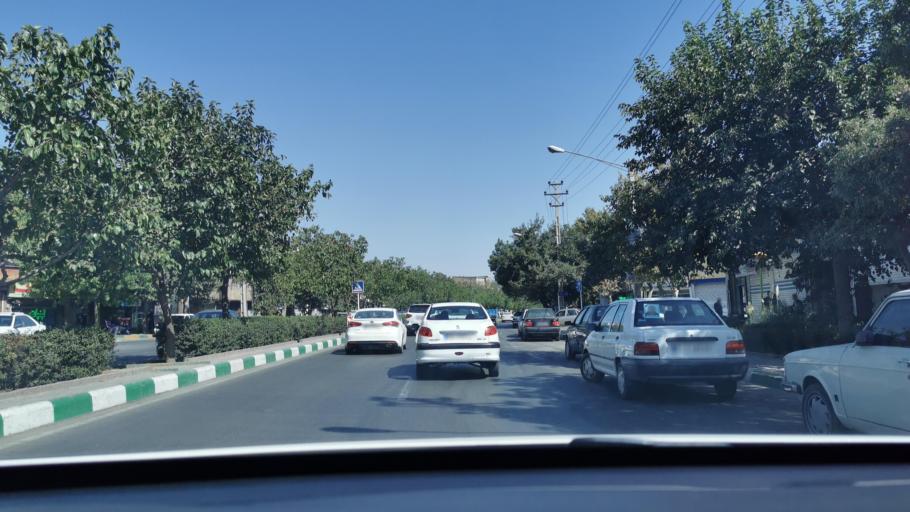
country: IR
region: Razavi Khorasan
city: Mashhad
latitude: 36.3388
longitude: 59.6253
